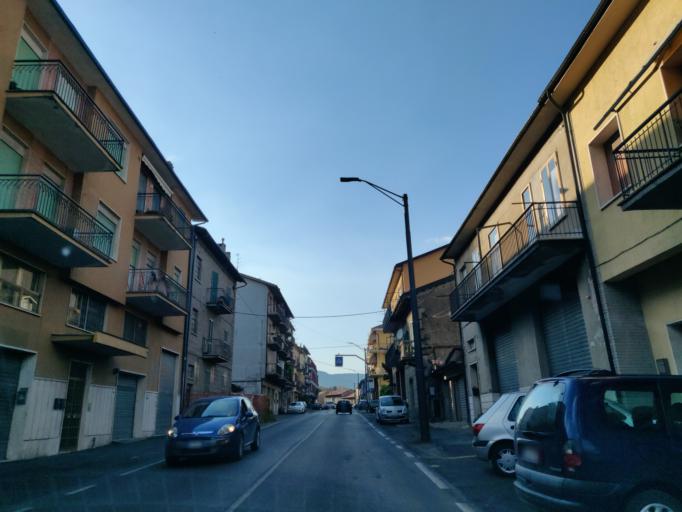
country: IT
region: Tuscany
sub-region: Provincia di Siena
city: Abbadia San Salvatore
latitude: 42.8755
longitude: 11.6841
